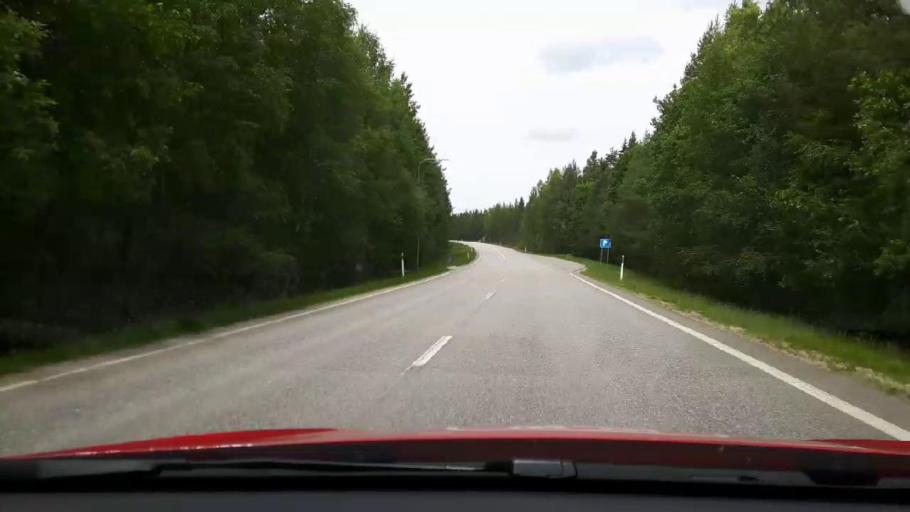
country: SE
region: Jaemtland
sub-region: Harjedalens Kommun
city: Sveg
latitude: 62.0733
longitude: 14.2701
